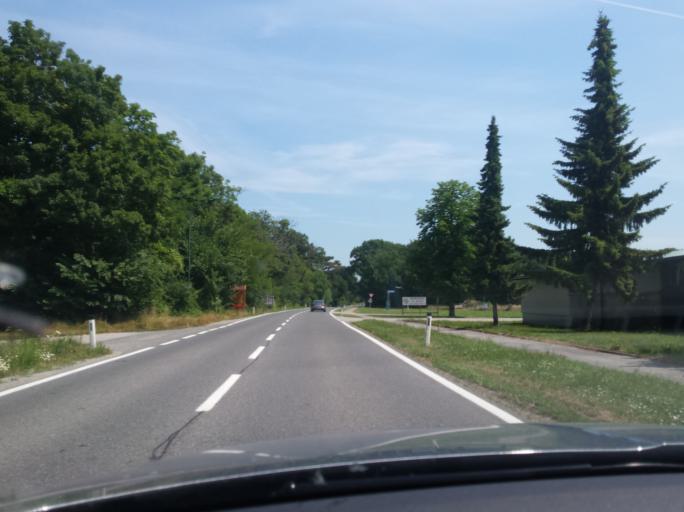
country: AT
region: Lower Austria
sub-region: Politischer Bezirk Bruck an der Leitha
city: Rohrau
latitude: 48.0596
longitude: 16.8475
